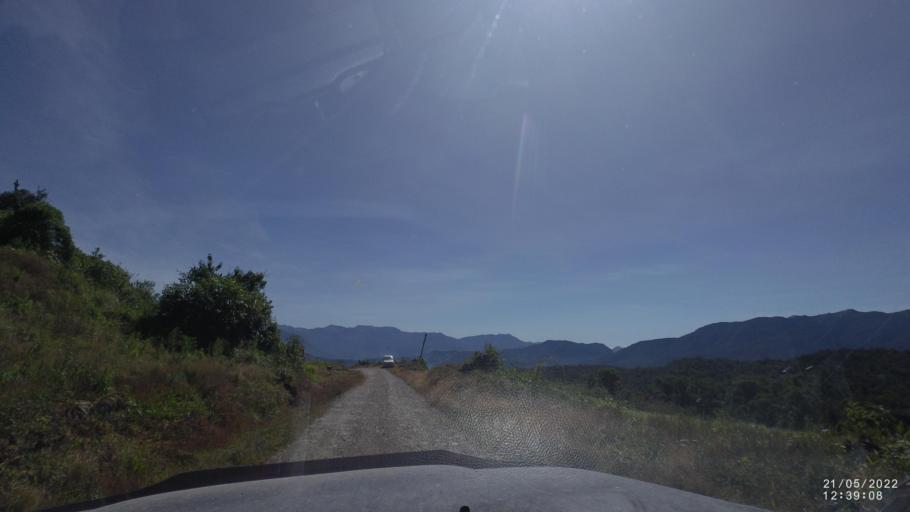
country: BO
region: Cochabamba
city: Colomi
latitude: -17.1984
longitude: -65.9216
